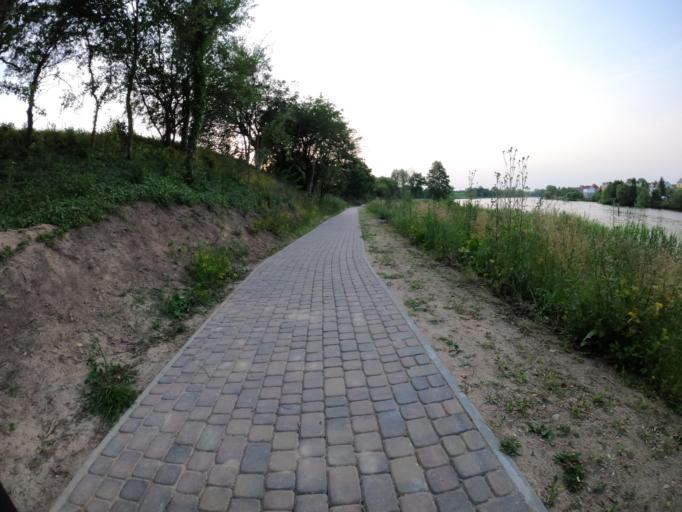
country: PL
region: West Pomeranian Voivodeship
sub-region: Powiat choszczenski
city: Pelczyce
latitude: 53.0392
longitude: 15.2975
